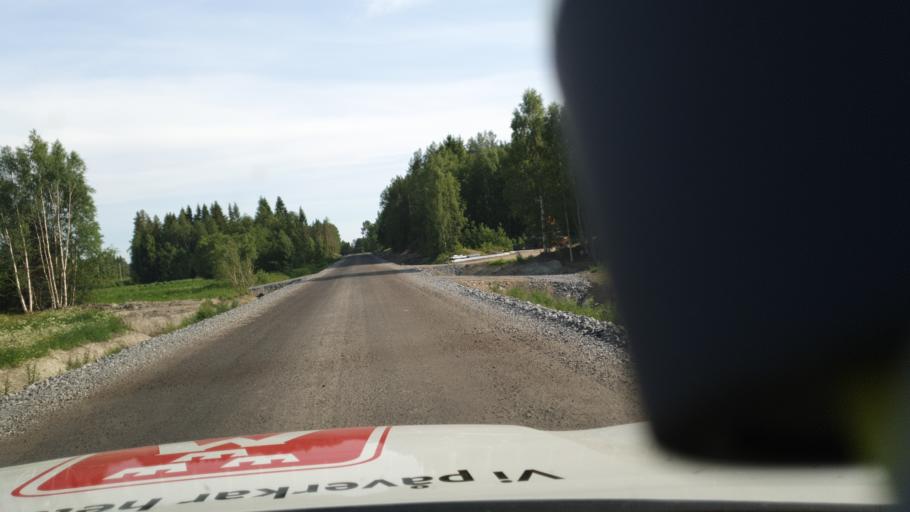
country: SE
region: Vaesterbotten
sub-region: Robertsfors Kommun
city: Robertsfors
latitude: 64.2927
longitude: 21.0326
